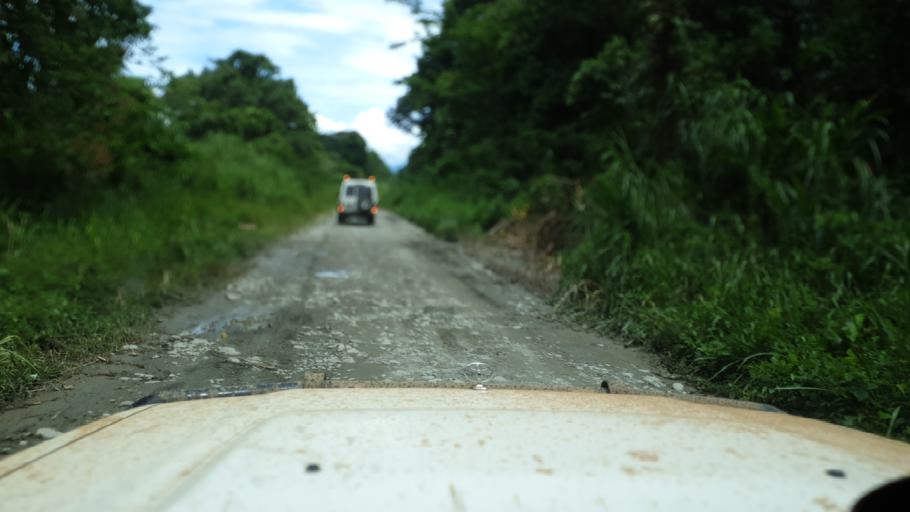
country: PG
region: Northern Province
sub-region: Sohe
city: Kokoda
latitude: -8.9162
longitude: 147.9147
